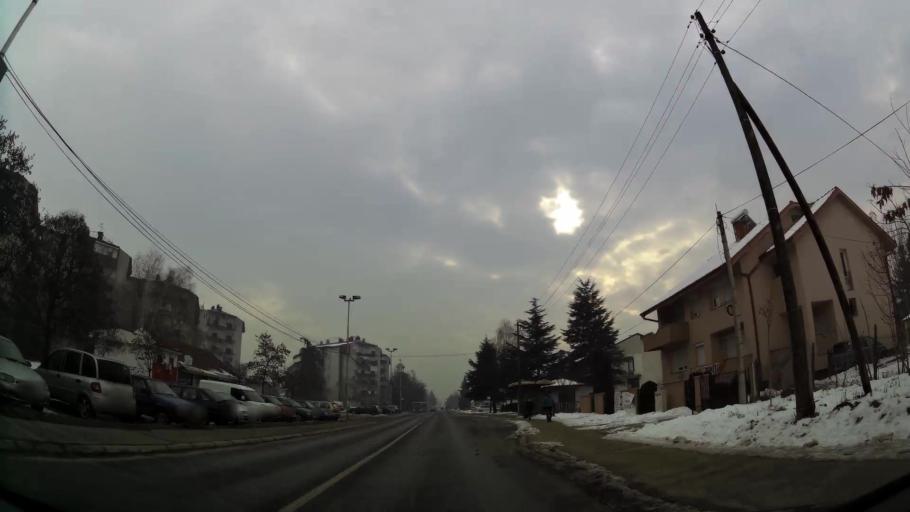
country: MK
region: Saraj
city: Saraj
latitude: 42.0198
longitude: 21.3533
